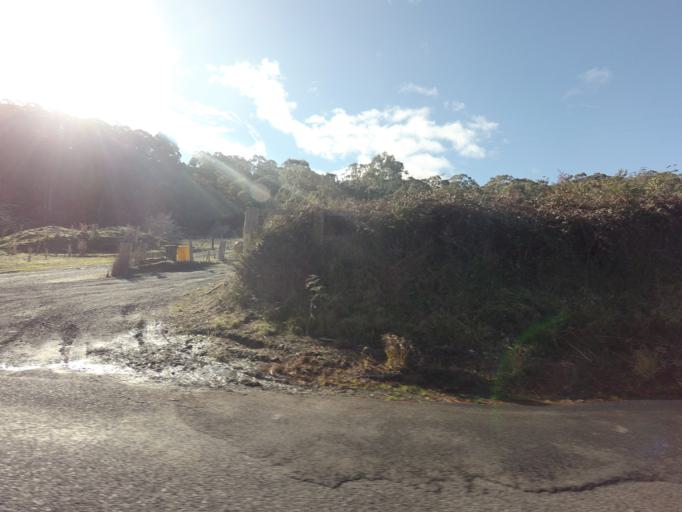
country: AU
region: Tasmania
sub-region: Glenorchy
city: Granton
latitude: -42.8054
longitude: 147.1646
